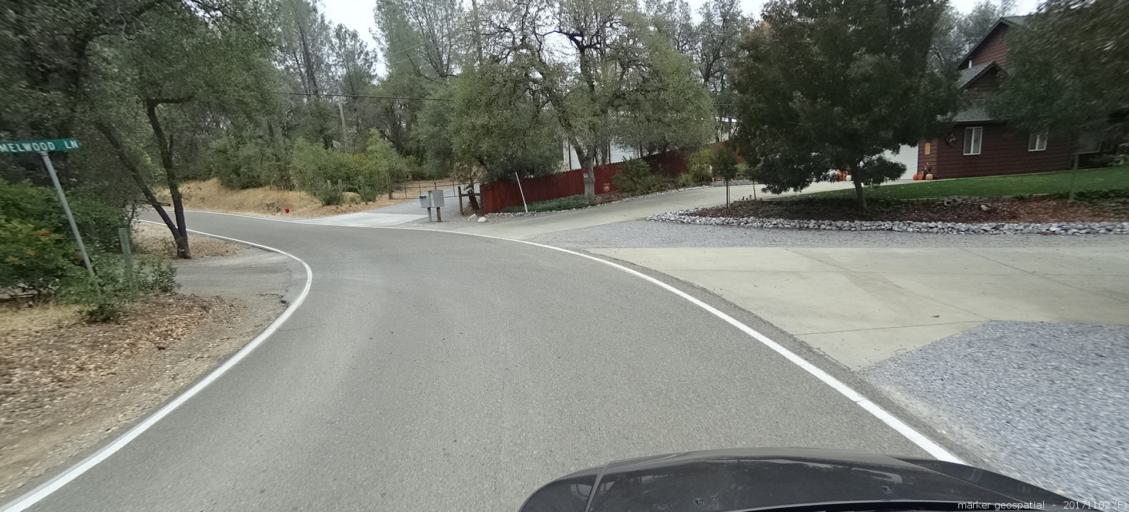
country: US
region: California
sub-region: Shasta County
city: Central Valley (historical)
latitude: 40.6412
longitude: -122.4029
